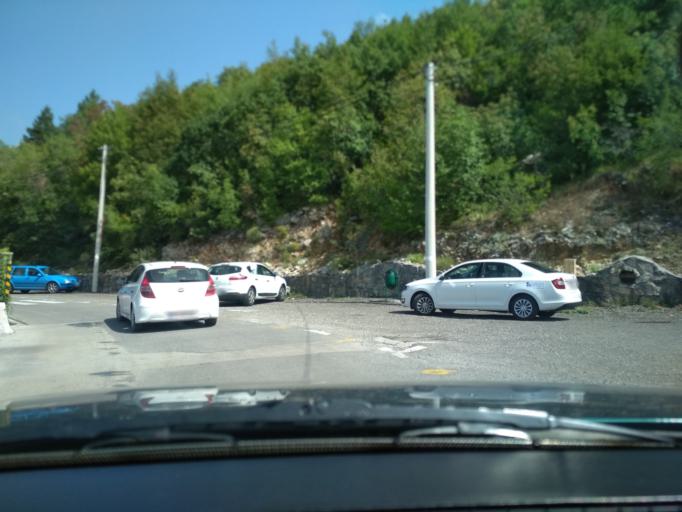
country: ME
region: Kotor
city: Kotor
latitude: 42.4197
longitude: 18.7945
